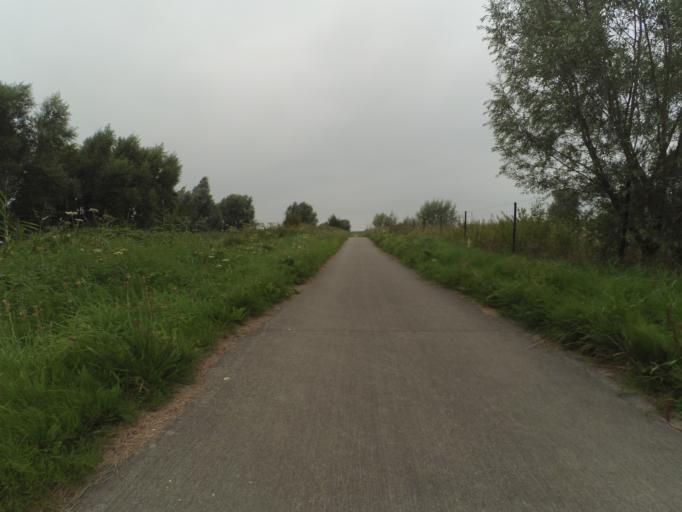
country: NL
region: Flevoland
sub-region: Gemeente Almere
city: Almere Stad
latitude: 52.4315
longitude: 5.2585
